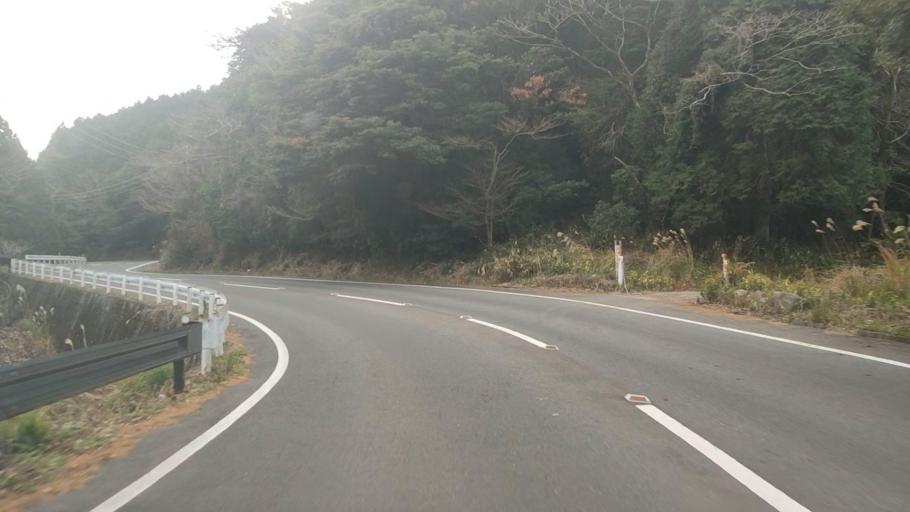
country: JP
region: Nagasaki
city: Shimabara
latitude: 32.7203
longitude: 130.2473
